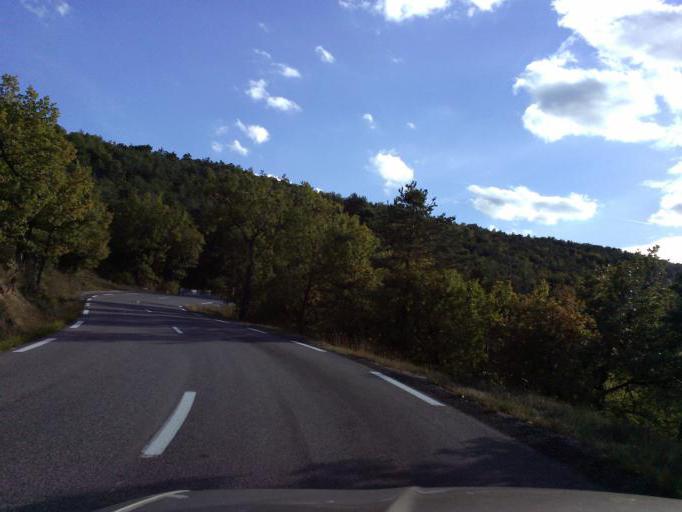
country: FR
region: Provence-Alpes-Cote d'Azur
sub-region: Departement des Alpes-de-Haute-Provence
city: Riez
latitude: 43.9013
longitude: 6.1387
